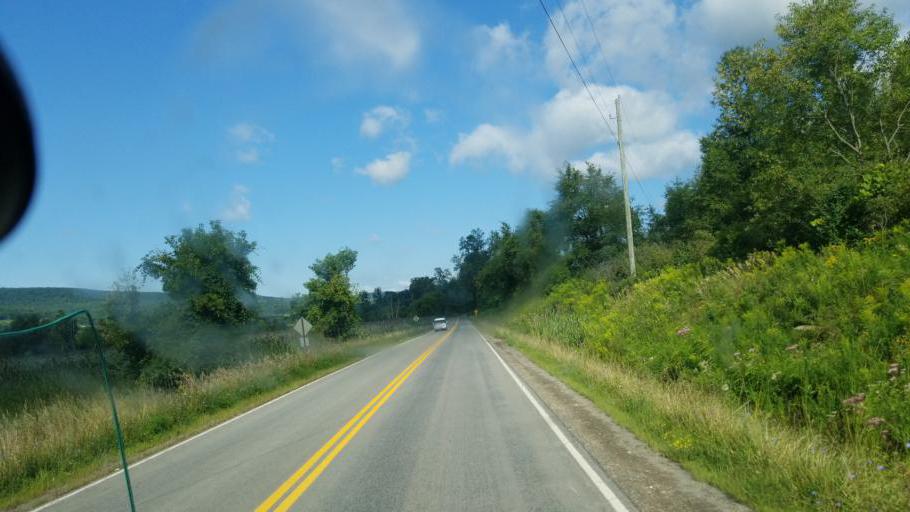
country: US
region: New York
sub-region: Steuben County
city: Canisteo
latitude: 42.2935
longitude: -77.6231
